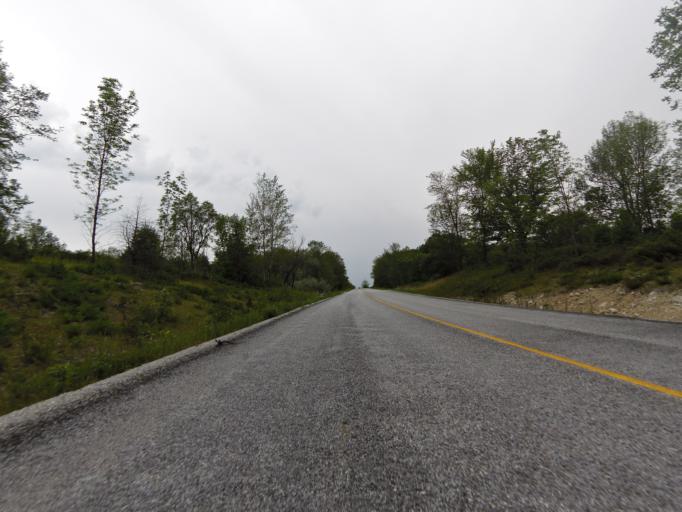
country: CA
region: Ontario
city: Perth
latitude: 44.8868
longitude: -76.5173
